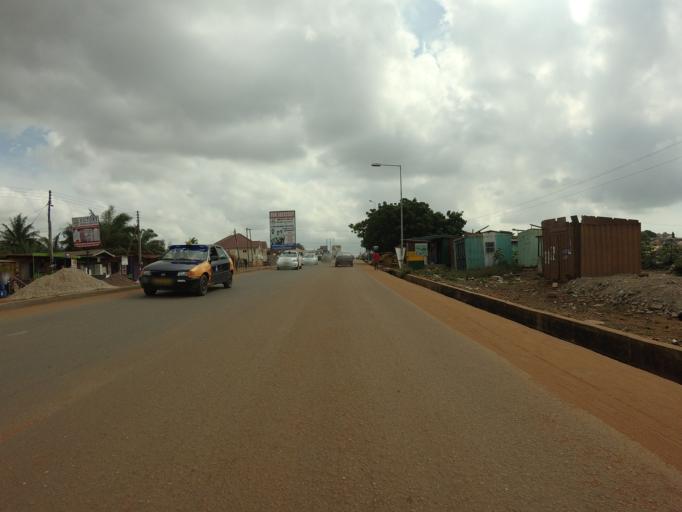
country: GH
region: Greater Accra
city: Teshi Old Town
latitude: 5.6045
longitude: -0.1194
